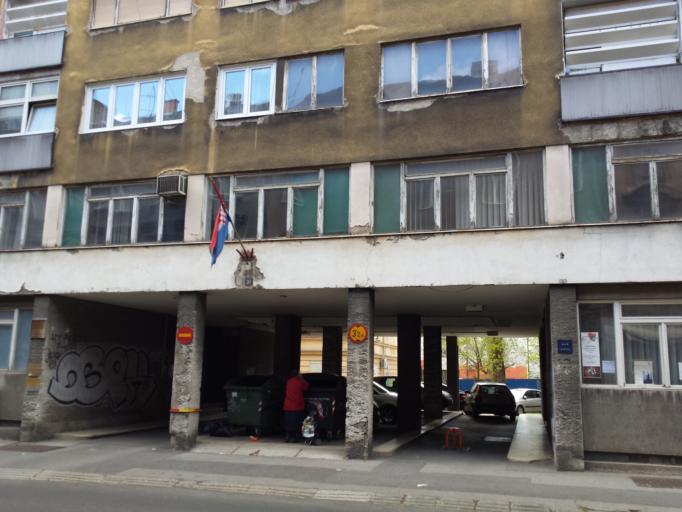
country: HR
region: Grad Zagreb
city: Zagreb - Centar
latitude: 45.8103
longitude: 15.9818
